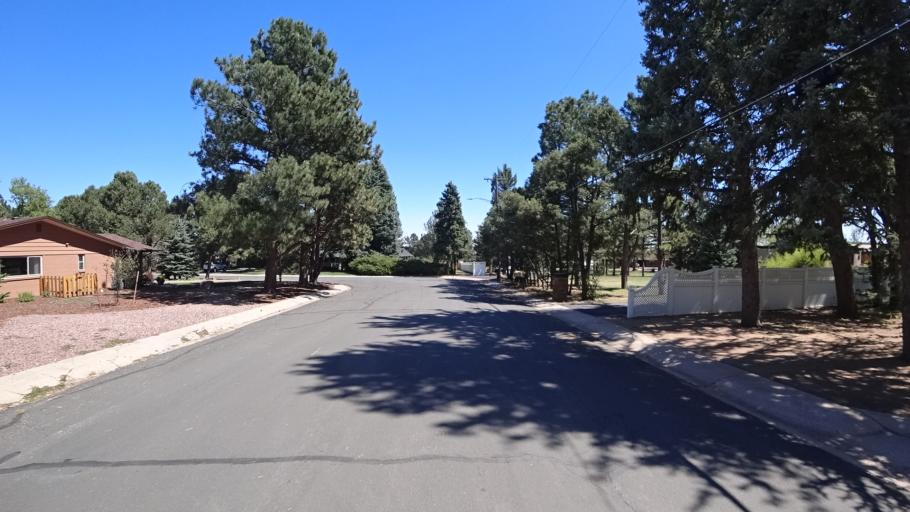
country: US
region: Colorado
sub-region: El Paso County
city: Colorado Springs
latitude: 38.7850
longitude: -104.8329
